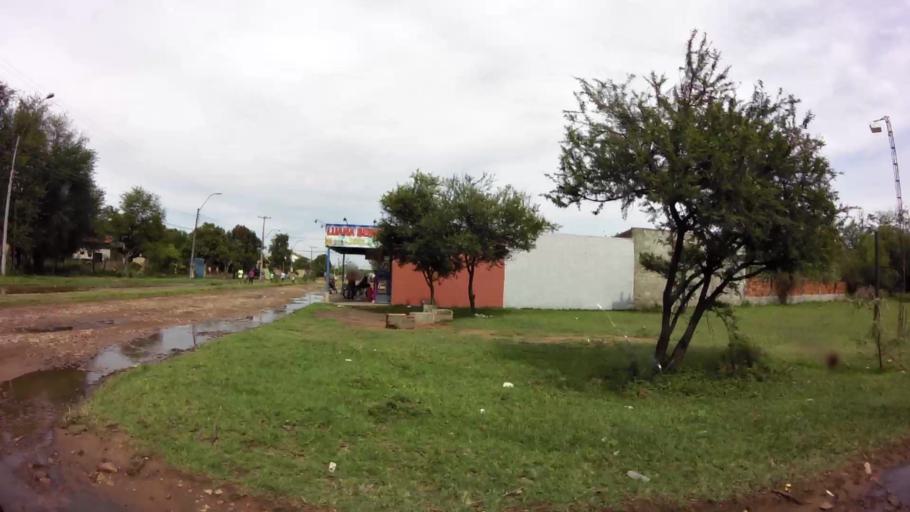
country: PY
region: Central
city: Limpio
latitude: -25.1665
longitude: -57.4842
